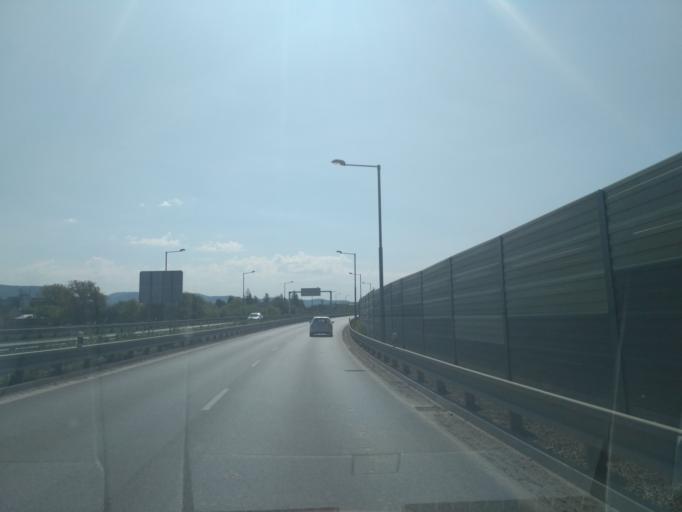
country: SK
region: Presovsky
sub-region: Okres Presov
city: Presov
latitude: 48.9824
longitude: 21.2361
